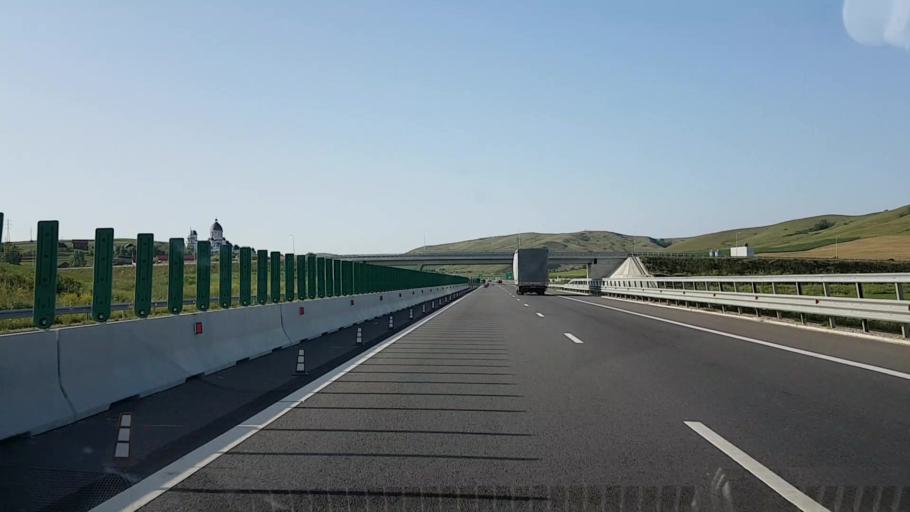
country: RO
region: Alba
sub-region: Comuna Unirea
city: Unirea
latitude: 46.4327
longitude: 23.7978
